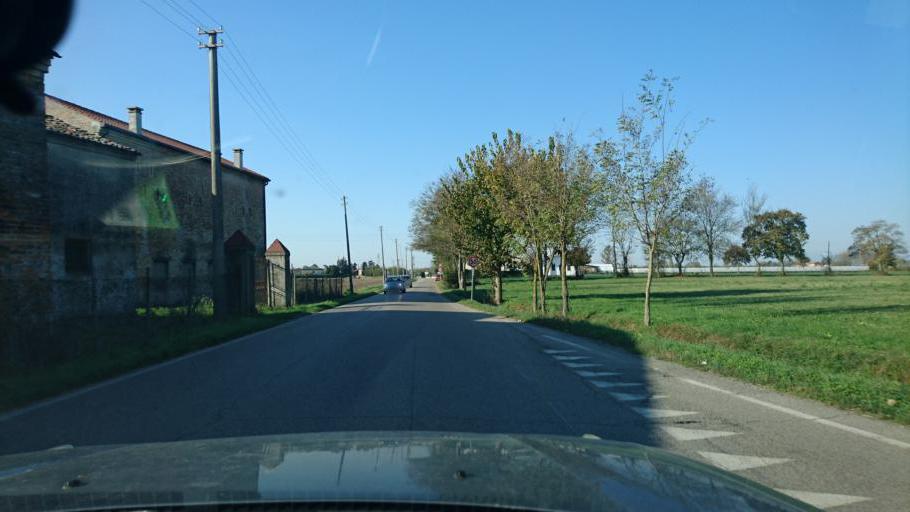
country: IT
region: Veneto
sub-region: Provincia di Padova
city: Ospedaletto Euganeo
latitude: 45.2131
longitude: 11.5973
